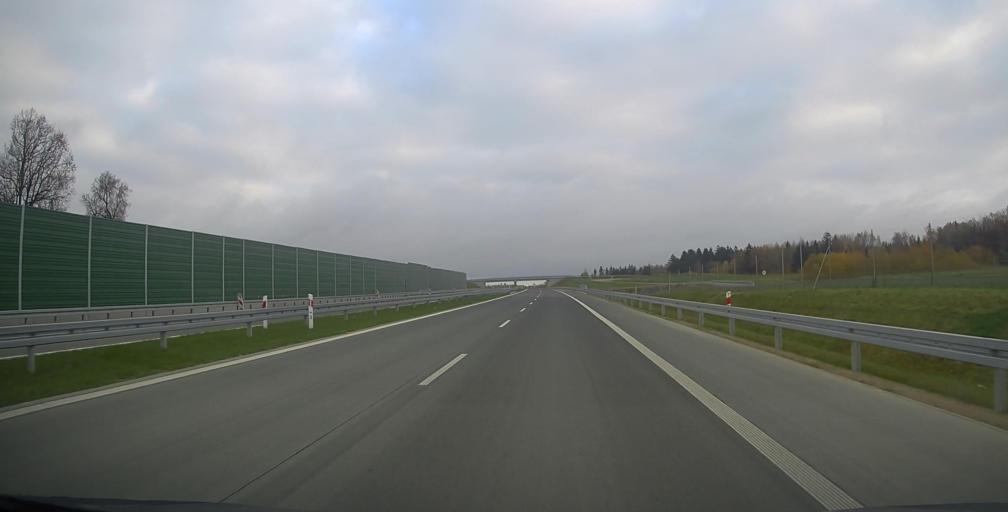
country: PL
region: Podlasie
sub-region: Powiat suwalski
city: Raczki
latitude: 53.9221
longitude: 22.7465
